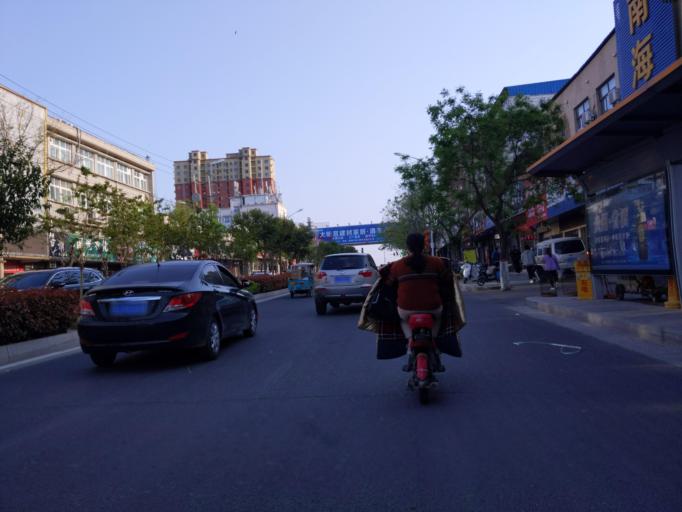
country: CN
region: Henan Sheng
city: Puyang Chengguanzhen
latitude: 35.6997
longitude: 115.0162
